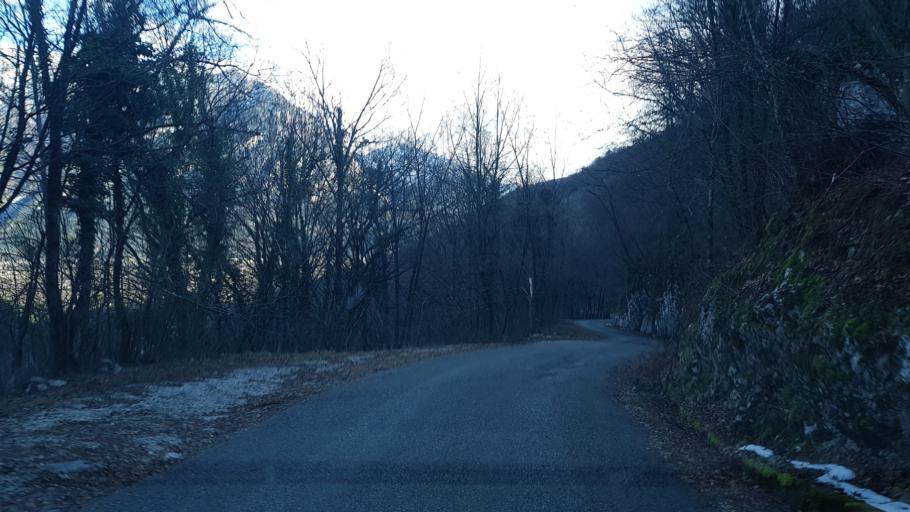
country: IT
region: Friuli Venezia Giulia
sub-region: Provincia di Udine
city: Trasaghis
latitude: 46.2905
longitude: 13.0360
